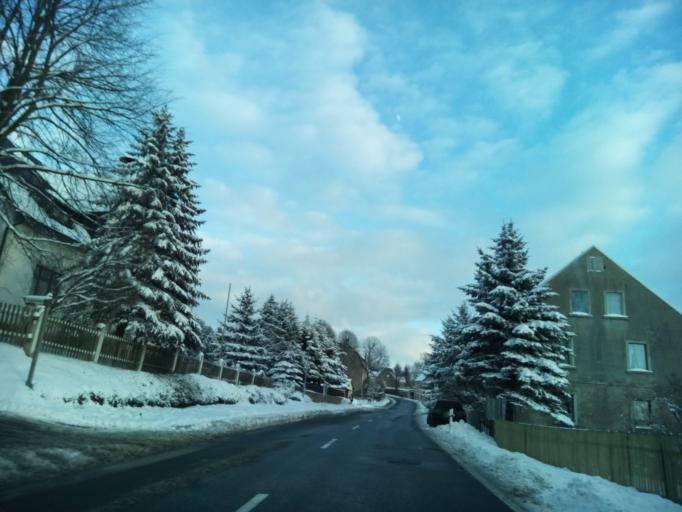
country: DE
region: Saxony
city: Bornichen
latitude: 50.7662
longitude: 13.1199
